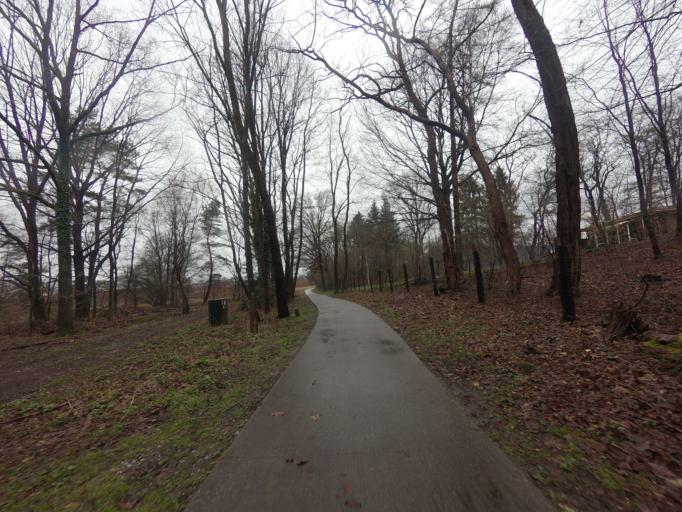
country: NL
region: Gelderland
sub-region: Gemeente Nunspeet
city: Nunspeet
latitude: 52.3274
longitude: 5.8182
